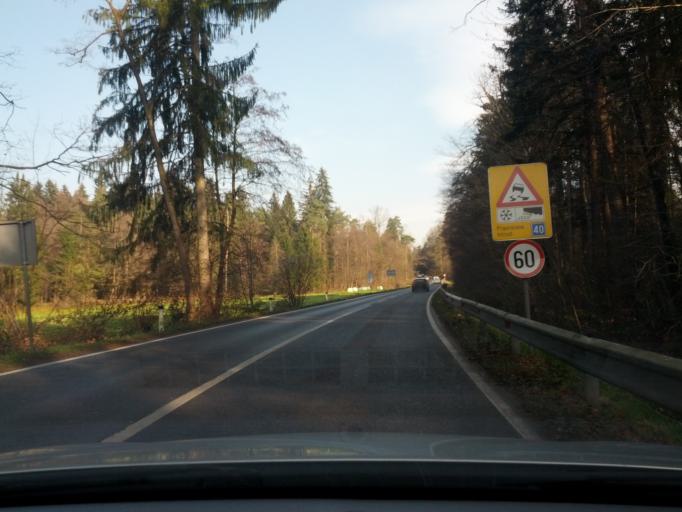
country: SI
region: Ljubljana
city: Ljubljana
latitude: 46.0598
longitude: 14.4665
